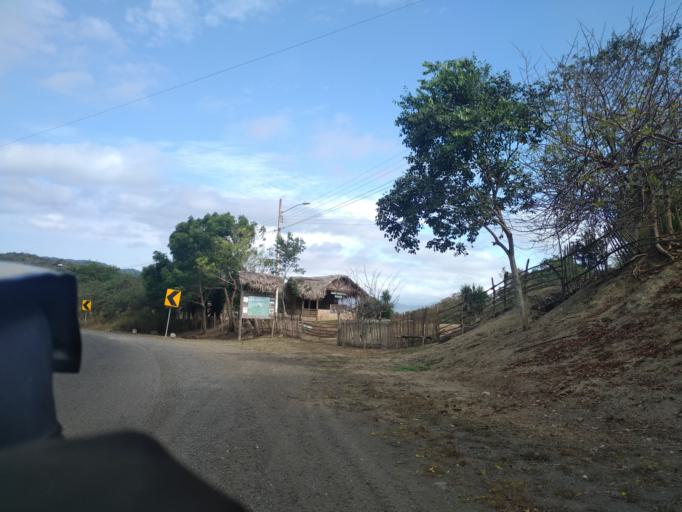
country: EC
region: Manabi
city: Jipijapa
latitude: -1.4380
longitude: -80.7563
